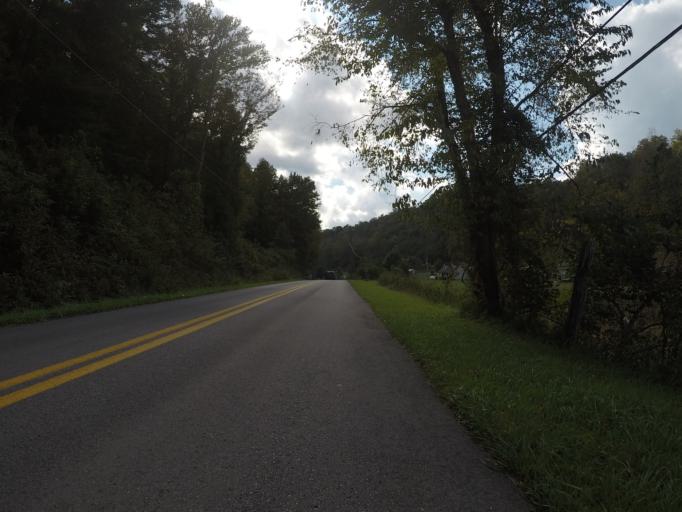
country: US
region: West Virginia
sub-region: Wayne County
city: Lavalette
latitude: 38.3590
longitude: -82.4330
